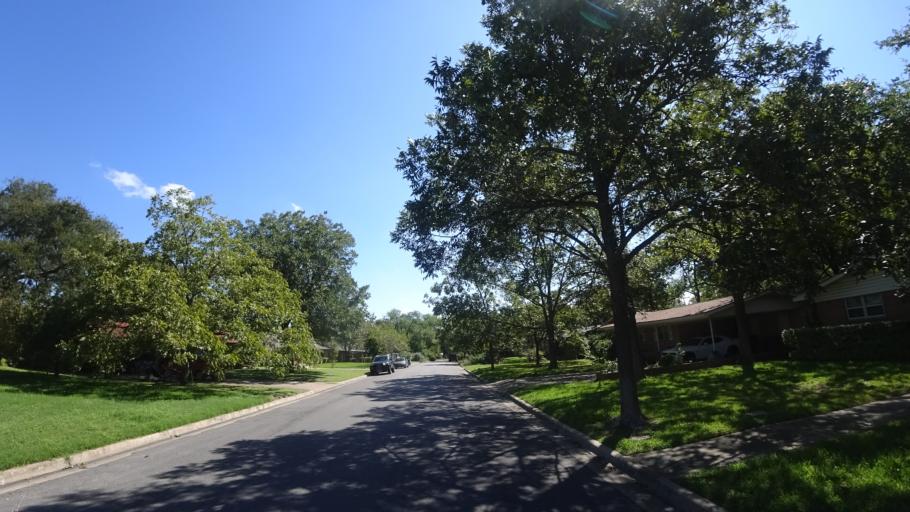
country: US
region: Texas
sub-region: Travis County
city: Austin
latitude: 30.3147
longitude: -97.6991
